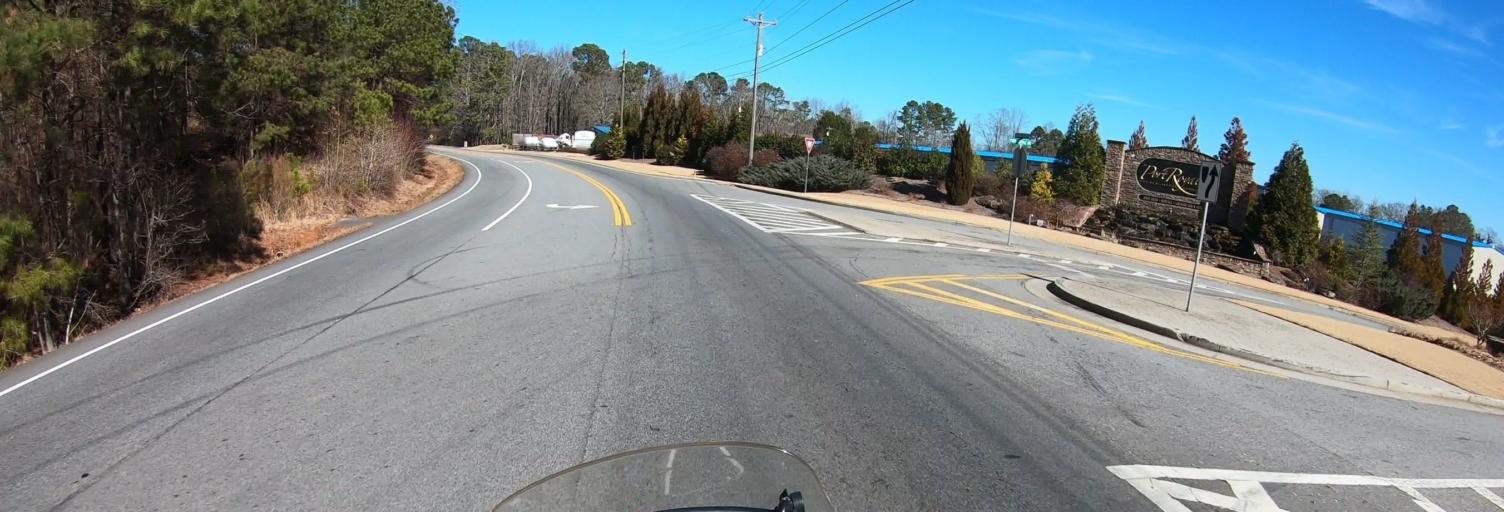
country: US
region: Georgia
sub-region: Hall County
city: Flowery Branch
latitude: 34.2516
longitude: -83.9675
